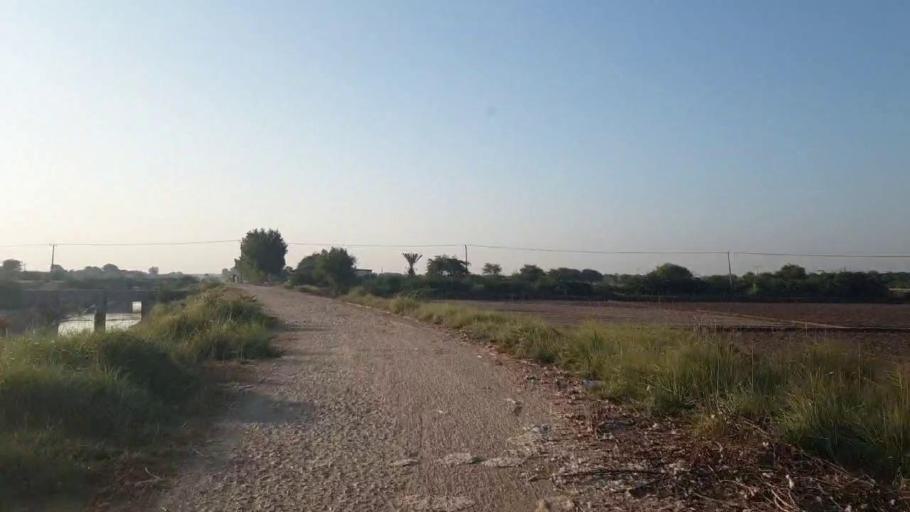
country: PK
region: Sindh
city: Badin
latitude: 24.6508
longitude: 68.7892
